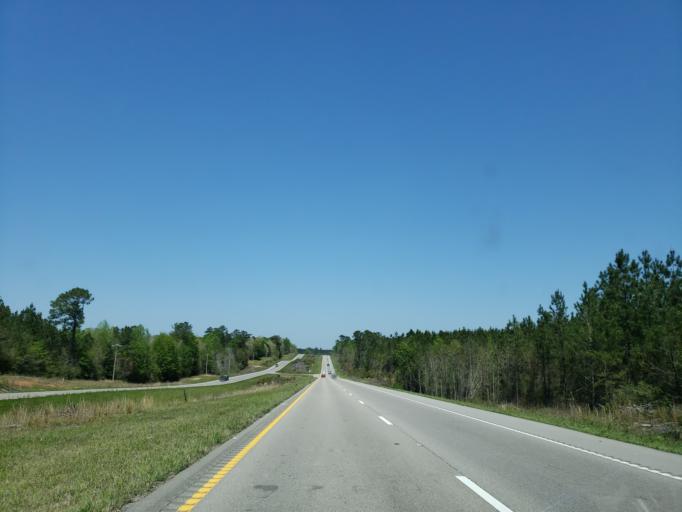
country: US
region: Mississippi
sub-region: Stone County
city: Wiggins
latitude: 30.9681
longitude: -89.1949
